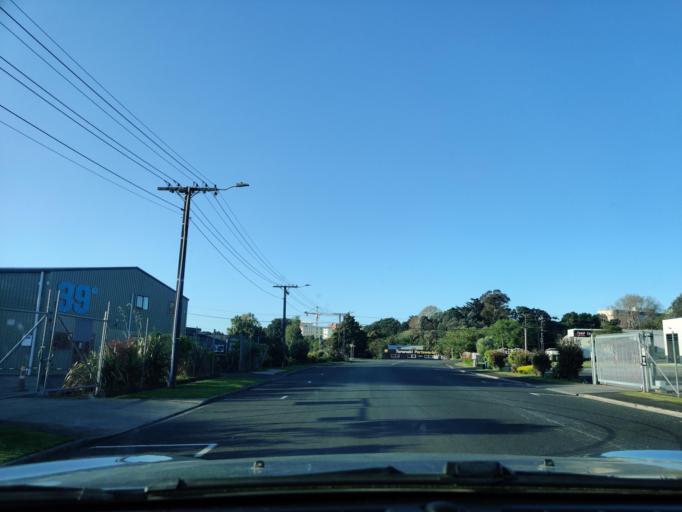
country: NZ
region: Taranaki
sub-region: New Plymouth District
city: New Plymouth
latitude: -39.0764
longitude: 174.0546
